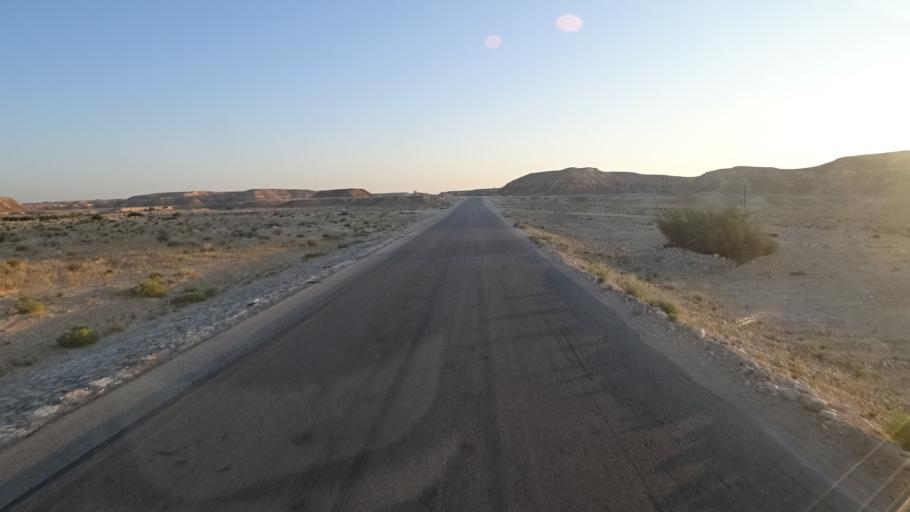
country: OM
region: Zufar
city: Salalah
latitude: 17.5049
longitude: 53.3636
